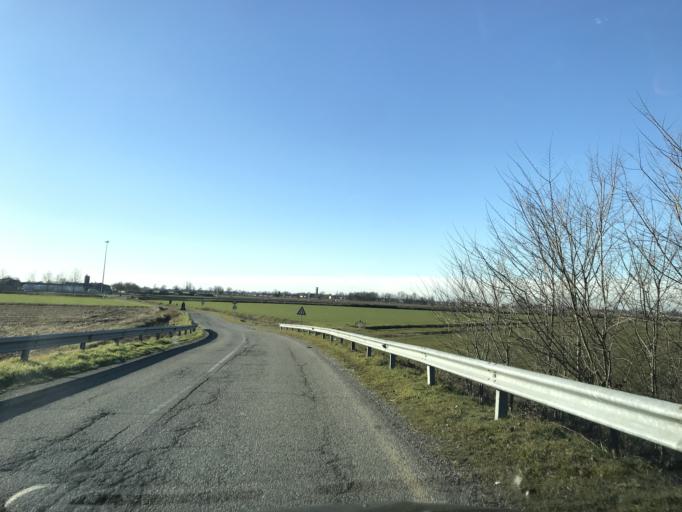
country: IT
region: Lombardy
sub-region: Provincia di Lodi
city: Borghetto Lodigiano
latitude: 45.2322
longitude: 9.5053
